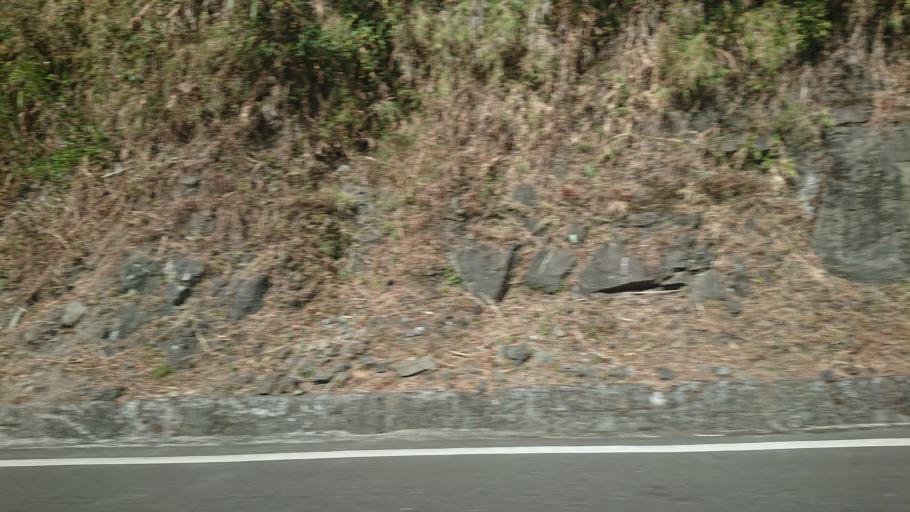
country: TW
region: Taiwan
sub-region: Chiayi
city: Jiayi Shi
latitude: 23.4648
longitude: 120.7283
